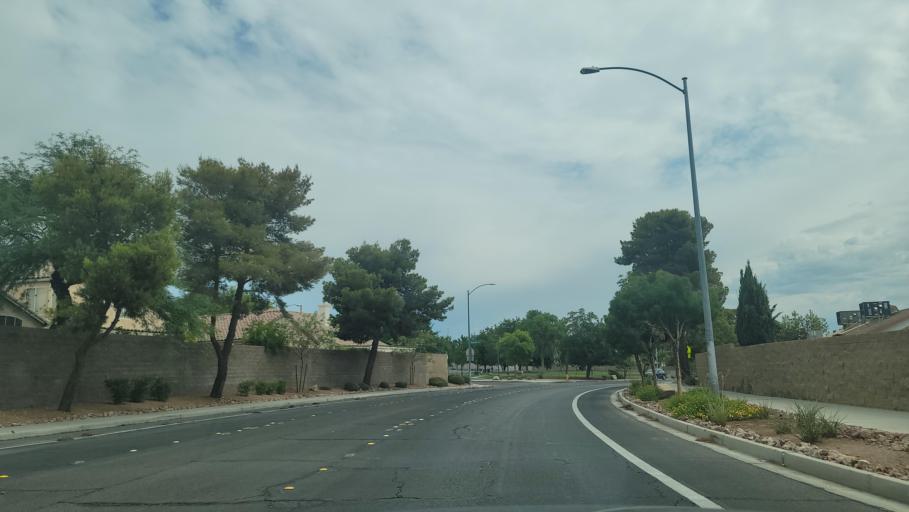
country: US
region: Nevada
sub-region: Clark County
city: Spring Valley
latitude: 36.1096
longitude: -115.2482
